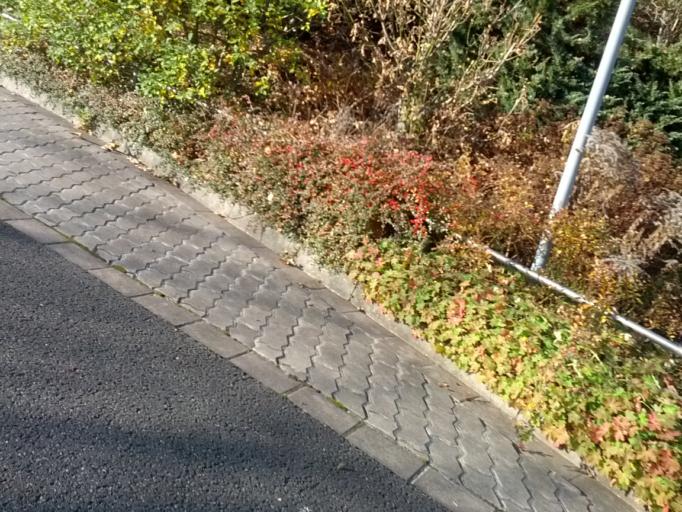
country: DE
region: Thuringia
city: Thal
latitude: 50.9188
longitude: 10.3927
